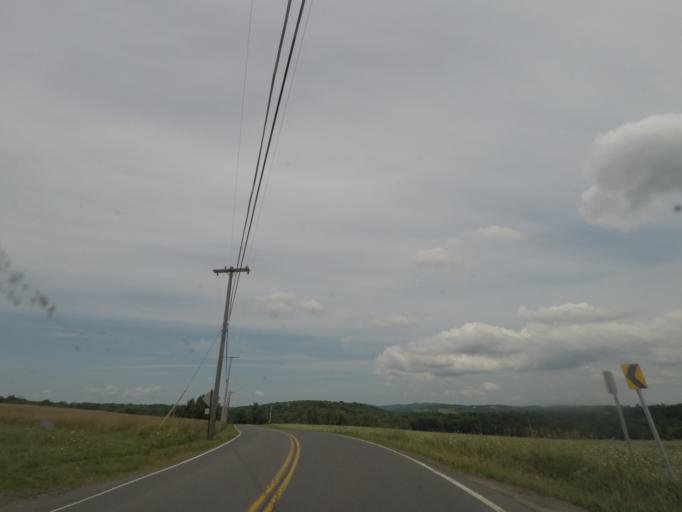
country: US
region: New York
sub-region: Rensselaer County
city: Wynantskill
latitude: 42.7107
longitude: -73.6073
